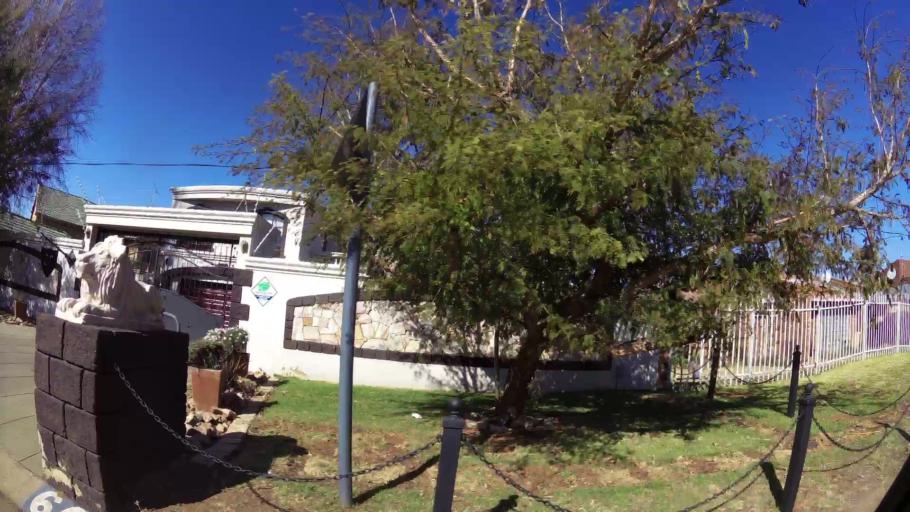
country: ZA
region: Gauteng
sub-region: Ekurhuleni Metropolitan Municipality
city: Germiston
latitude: -26.3010
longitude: 28.0996
